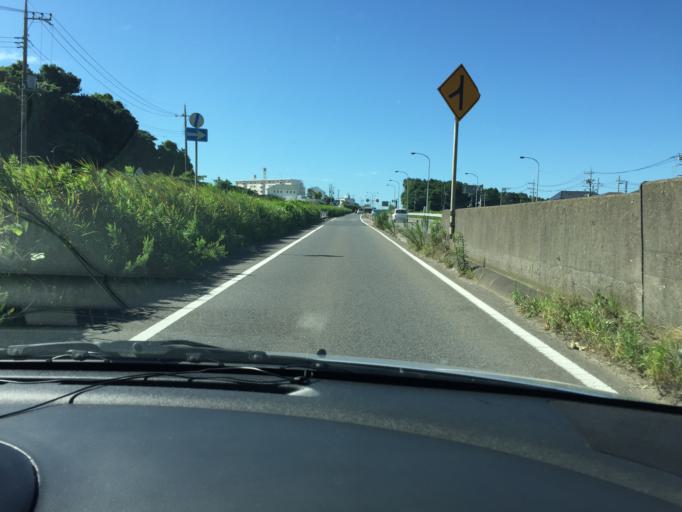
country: JP
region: Ibaraki
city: Naka
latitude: 36.0757
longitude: 140.1786
